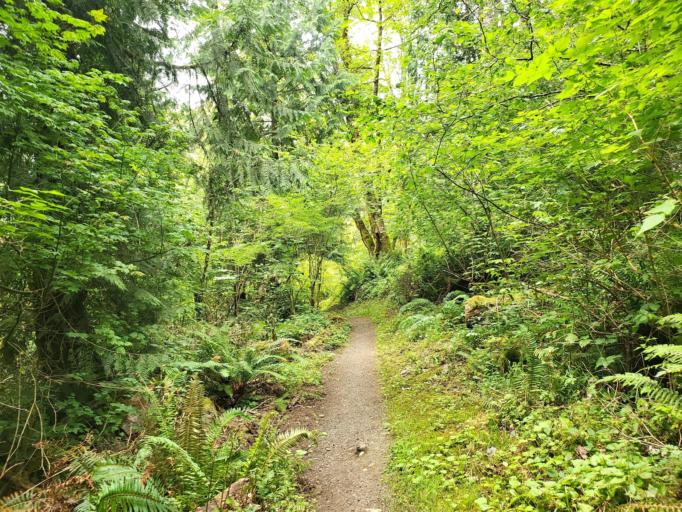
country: US
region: Washington
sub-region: King County
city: Newcastle
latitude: 47.5394
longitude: -122.1244
